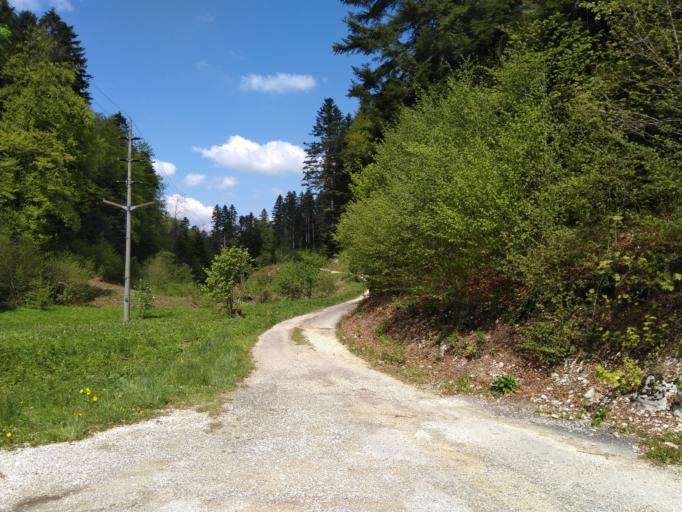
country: CH
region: Basel-Landschaft
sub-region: Bezirk Laufen
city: Wahlen
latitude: 47.3875
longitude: 7.4822
